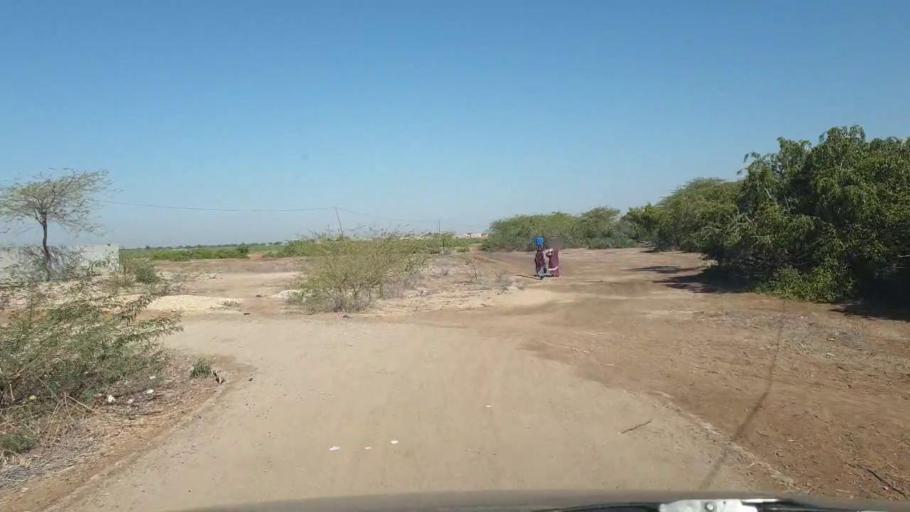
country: PK
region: Sindh
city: Umarkot
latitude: 25.3887
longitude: 69.6718
